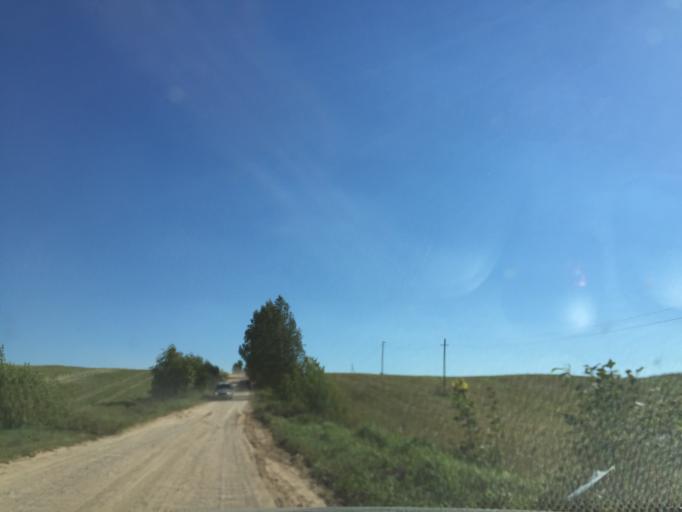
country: LT
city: Zarasai
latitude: 55.7942
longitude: 25.9527
